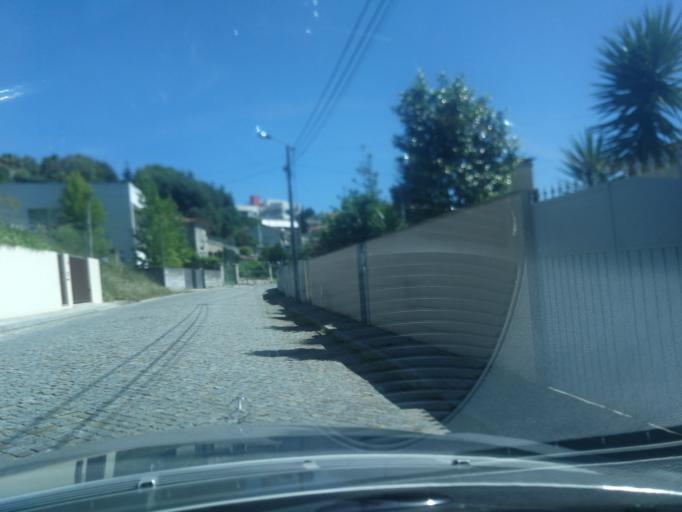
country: PT
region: Braga
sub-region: Braga
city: Adaufe
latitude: 41.5711
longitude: -8.4066
